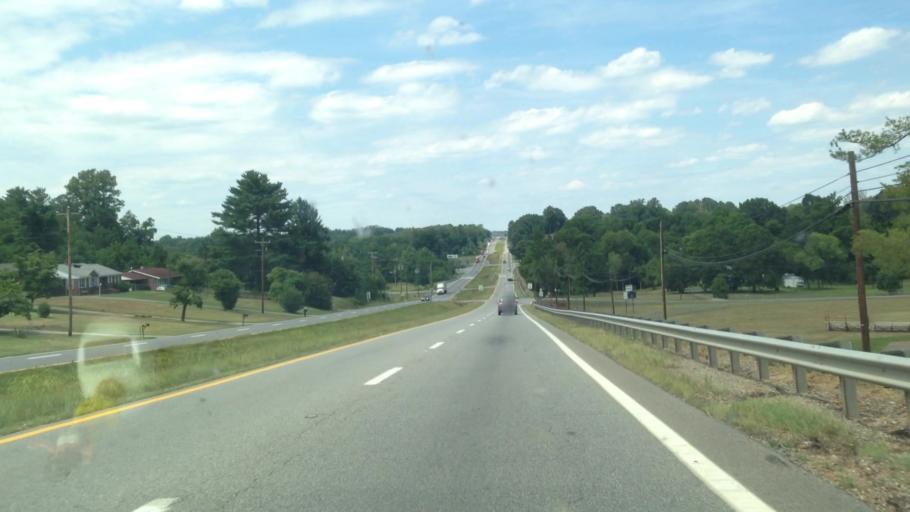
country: US
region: Virginia
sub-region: Henry County
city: Chatmoss
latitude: 36.6082
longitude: -79.8612
